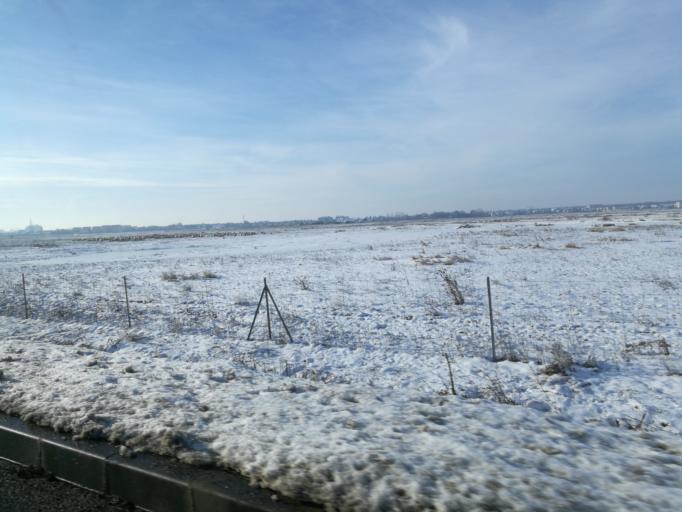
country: RO
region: Ilfov
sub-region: Voluntari City
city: Voluntari
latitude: 44.5049
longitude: 26.1583
